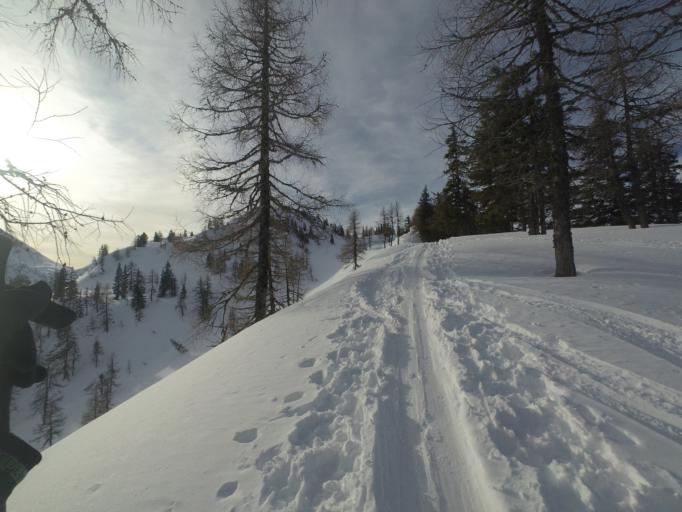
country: AT
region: Salzburg
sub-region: Politischer Bezirk Zell am See
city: Rauris
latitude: 47.2655
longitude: 13.0192
